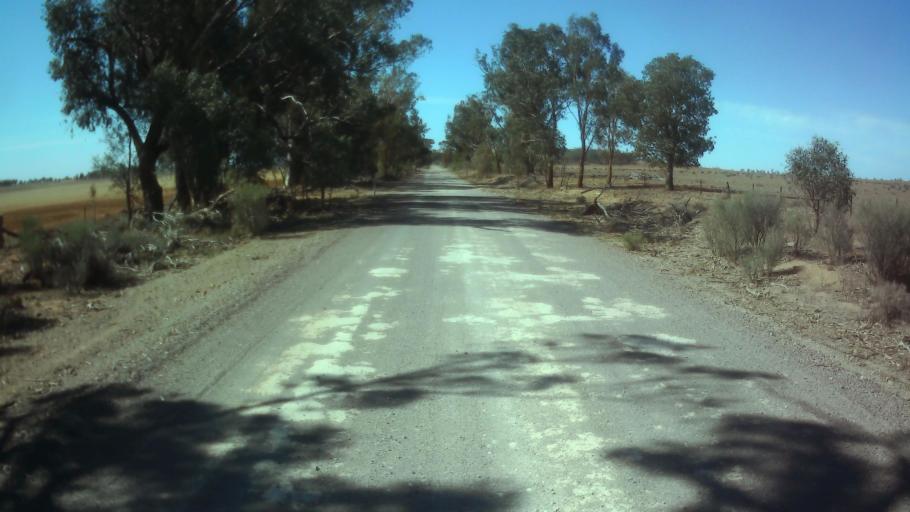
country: AU
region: New South Wales
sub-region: Forbes
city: Forbes
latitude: -33.7221
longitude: 147.7452
